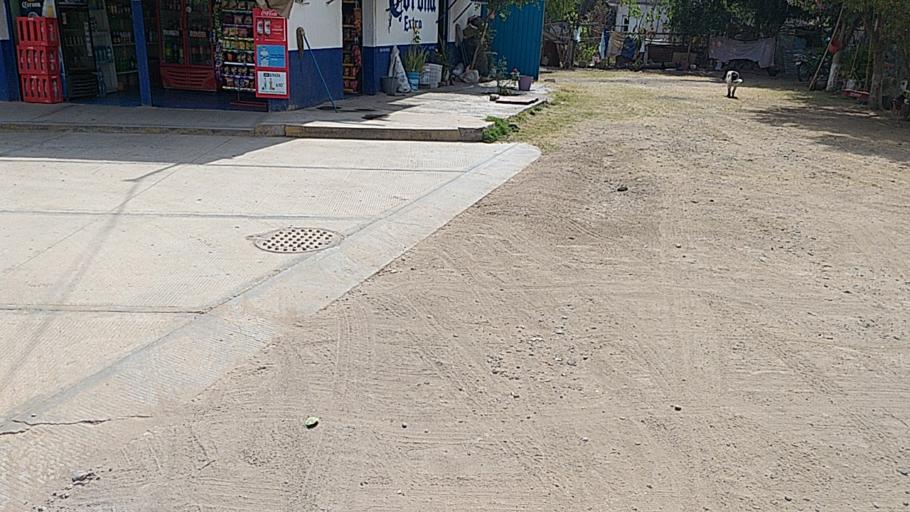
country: MX
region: Oaxaca
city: Ciudad de Huajuapam de Leon
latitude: 17.8127
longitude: -97.7647
